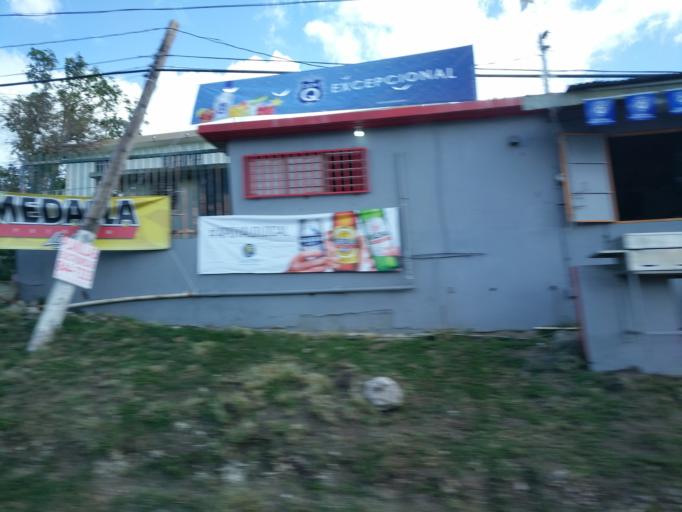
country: PR
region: Santa Isabel Municipio
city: El Ojo
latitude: 18.0247
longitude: -66.3697
